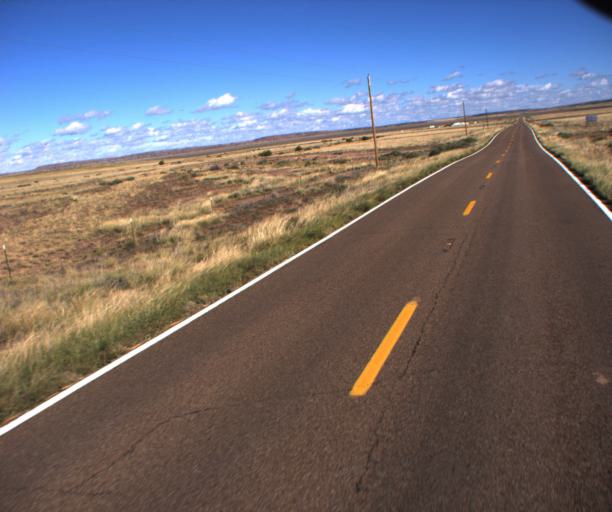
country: US
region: Arizona
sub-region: Apache County
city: Saint Johns
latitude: 34.5874
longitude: -109.3303
